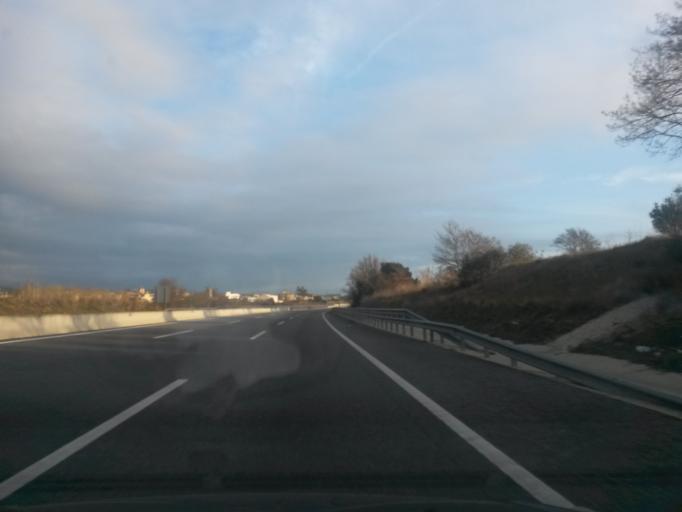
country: ES
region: Catalonia
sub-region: Provincia de Girona
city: Vilafant
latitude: 42.2408
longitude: 2.9378
